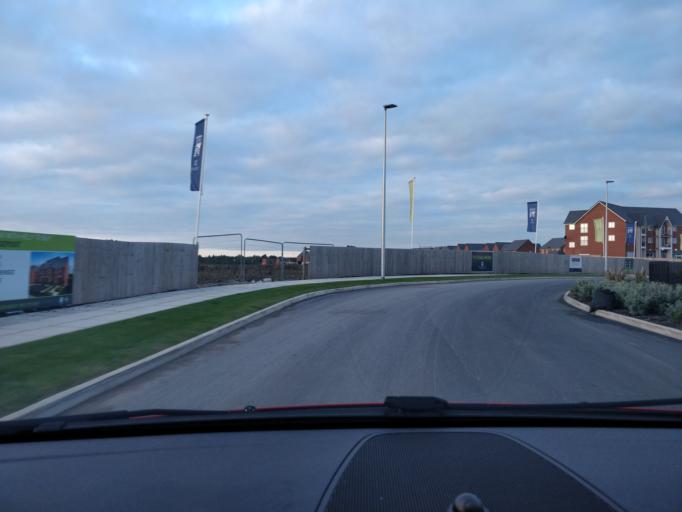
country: GB
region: England
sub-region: Sefton
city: Southport
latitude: 53.6269
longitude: -2.9835
